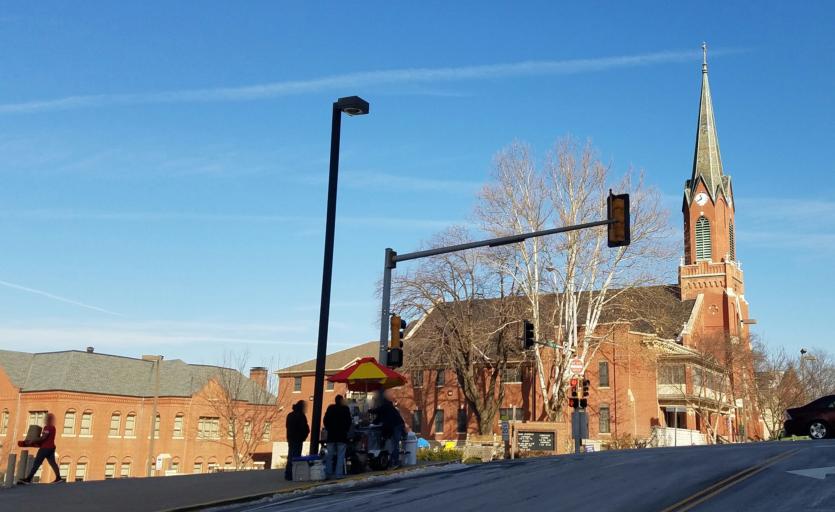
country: US
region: Missouri
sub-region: Cole County
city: Jefferson City
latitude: 38.5788
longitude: -92.1755
